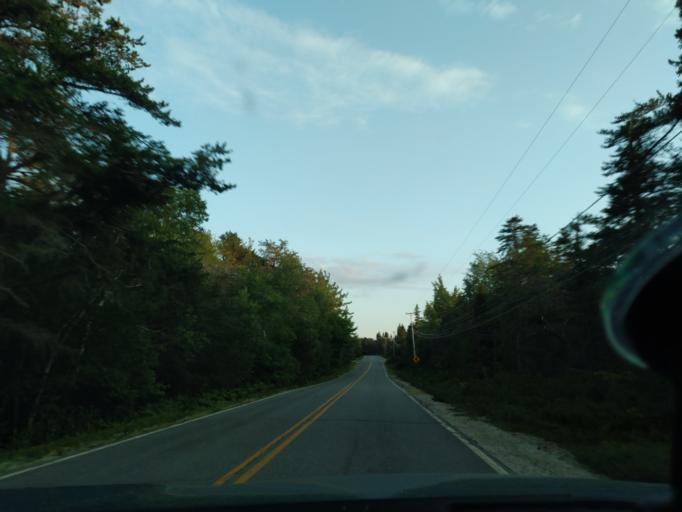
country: US
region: Maine
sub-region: Hancock County
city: Gouldsboro
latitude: 44.3810
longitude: -68.0364
